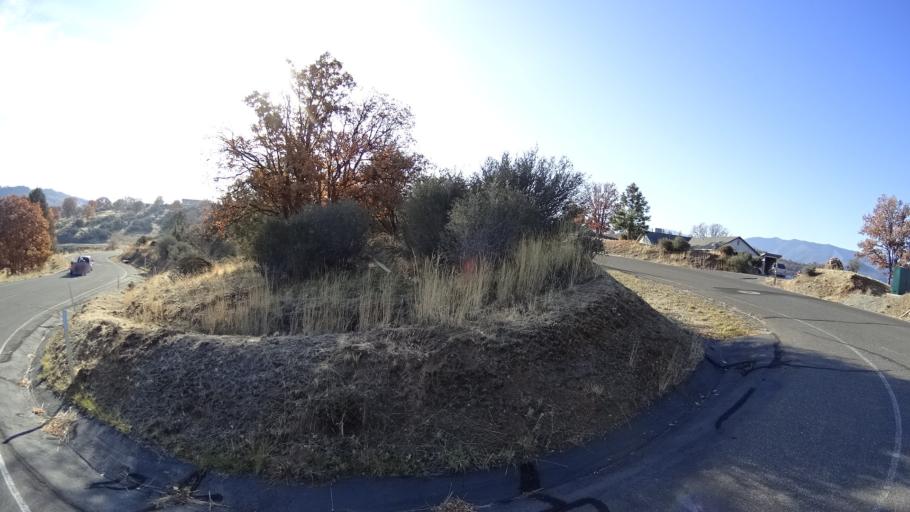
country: US
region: California
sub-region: Siskiyou County
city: Yreka
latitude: 41.7106
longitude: -122.6280
